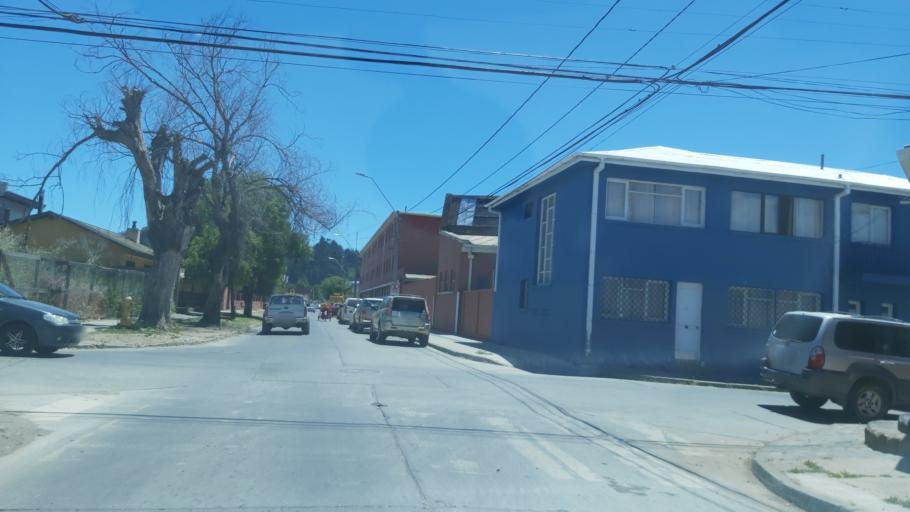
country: CL
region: Maule
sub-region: Provincia de Talca
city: Constitucion
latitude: -35.3317
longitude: -72.4065
